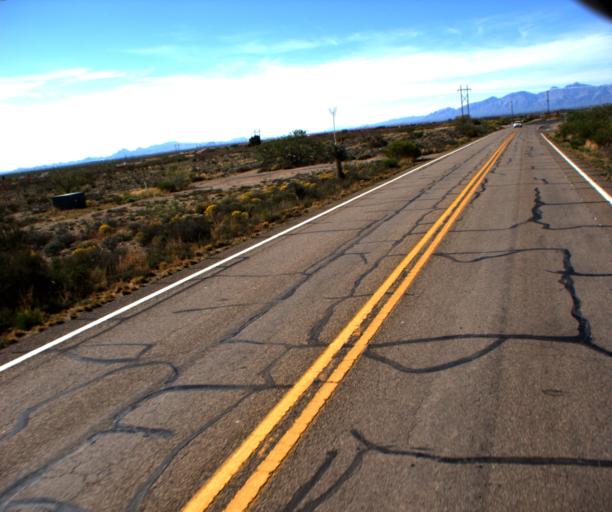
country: US
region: Arizona
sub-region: Pima County
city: Vail
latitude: 32.0016
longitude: -110.6887
